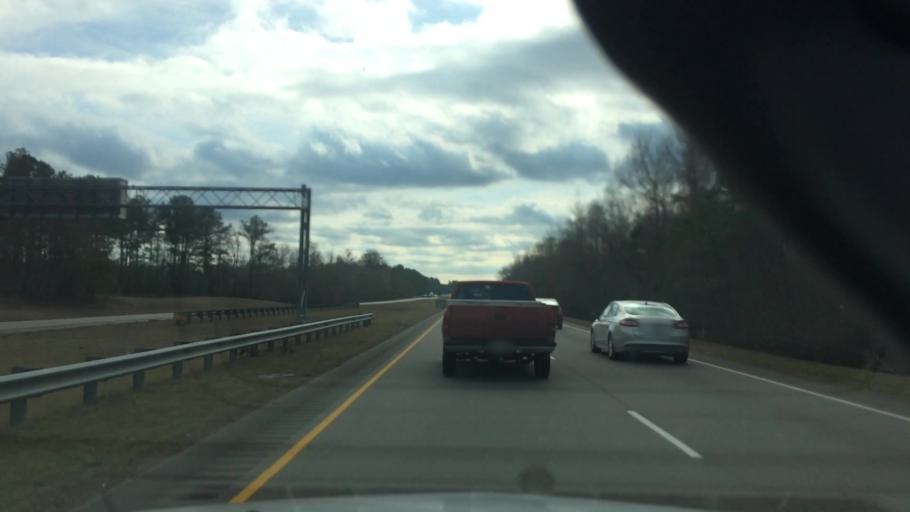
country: US
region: North Carolina
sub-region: Brunswick County
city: Leland
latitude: 34.1636
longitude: -78.0902
